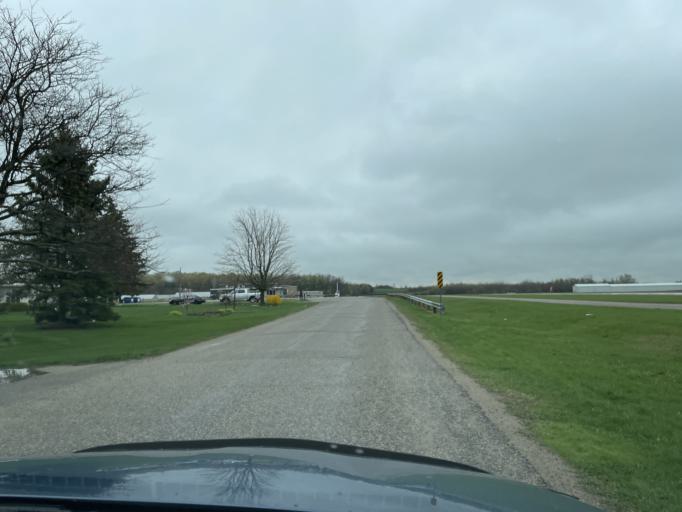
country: CA
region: Ontario
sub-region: Wellington County
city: Guelph
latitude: 43.5645
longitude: -80.1969
